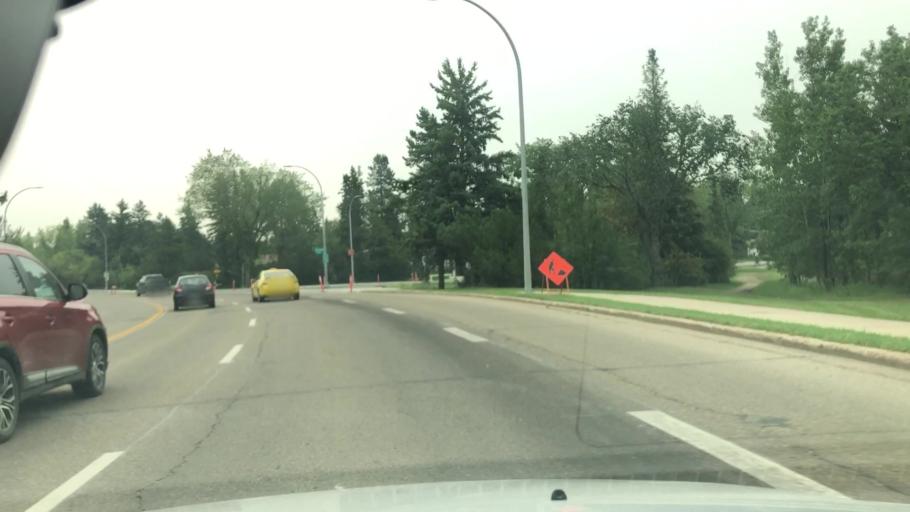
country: CA
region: Alberta
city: Edmonton
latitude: 53.5186
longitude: -113.5376
